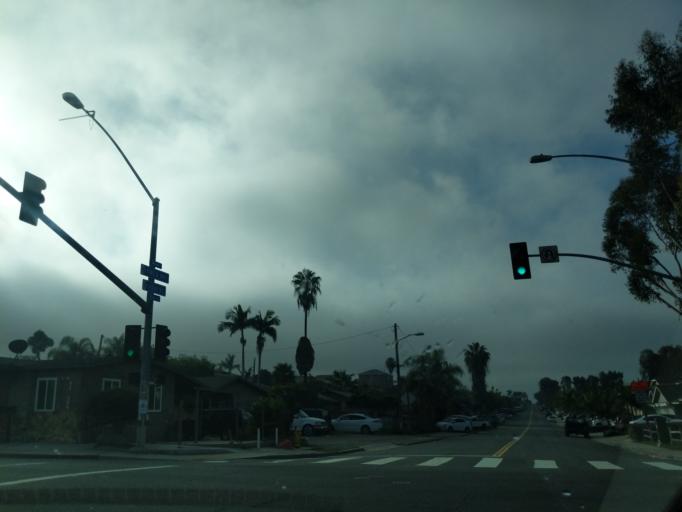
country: US
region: California
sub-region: San Diego County
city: National City
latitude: 32.7043
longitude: -117.0981
